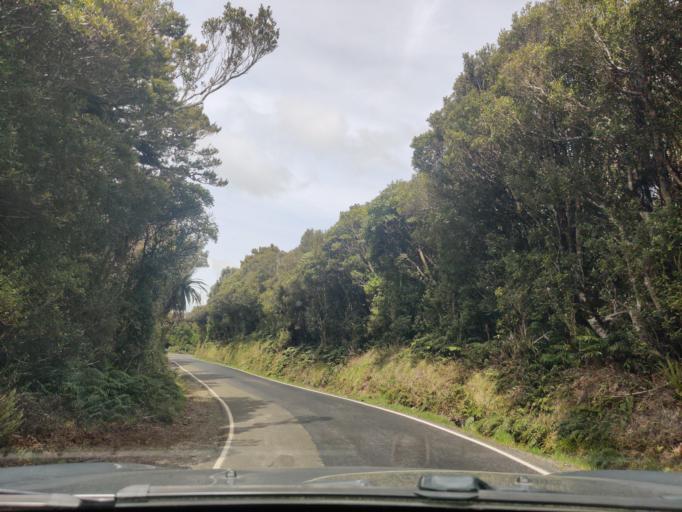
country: NZ
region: Taranaki
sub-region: South Taranaki District
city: Eltham
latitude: -39.3240
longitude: 174.1055
